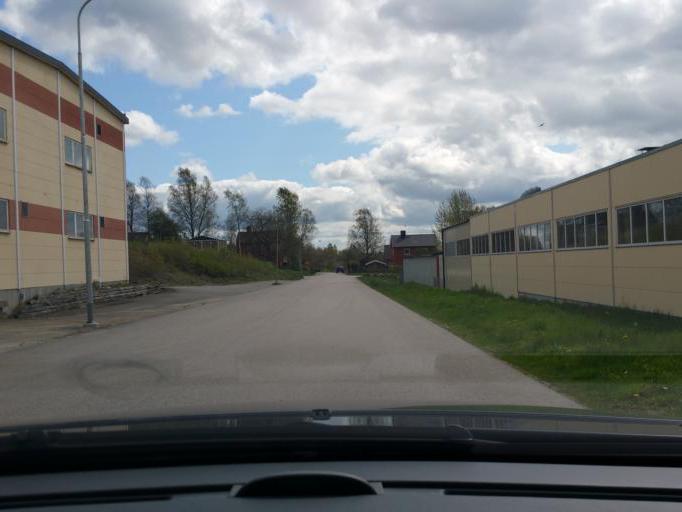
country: SE
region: Kronoberg
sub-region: Vaxjo Kommun
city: Lammhult
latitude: 57.1609
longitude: 14.5885
